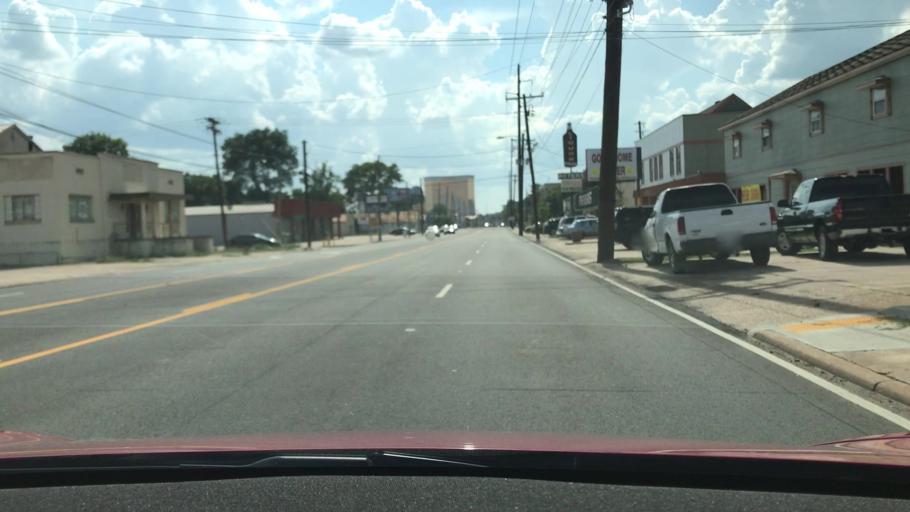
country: US
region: Louisiana
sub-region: Bossier Parish
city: Bossier City
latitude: 32.5159
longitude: -93.7216
